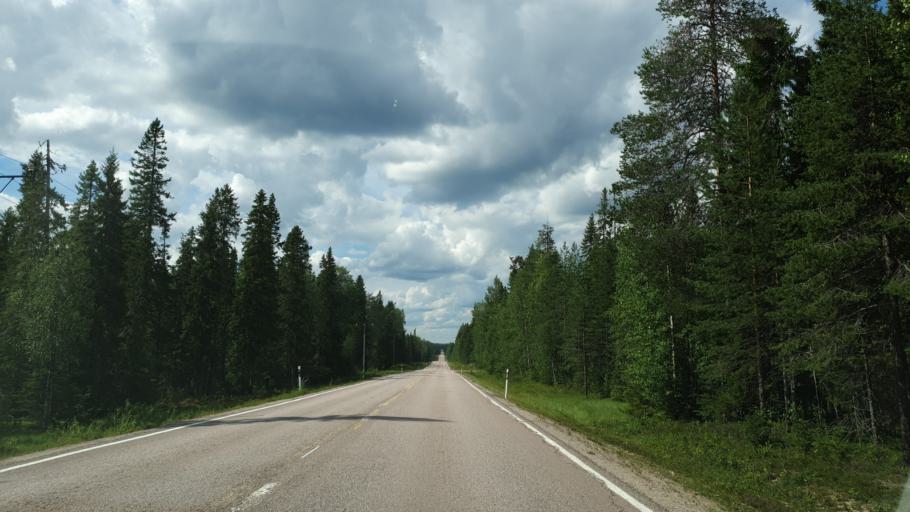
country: FI
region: Kainuu
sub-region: Kehys-Kainuu
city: Hyrynsalmi
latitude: 64.4625
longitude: 28.8540
